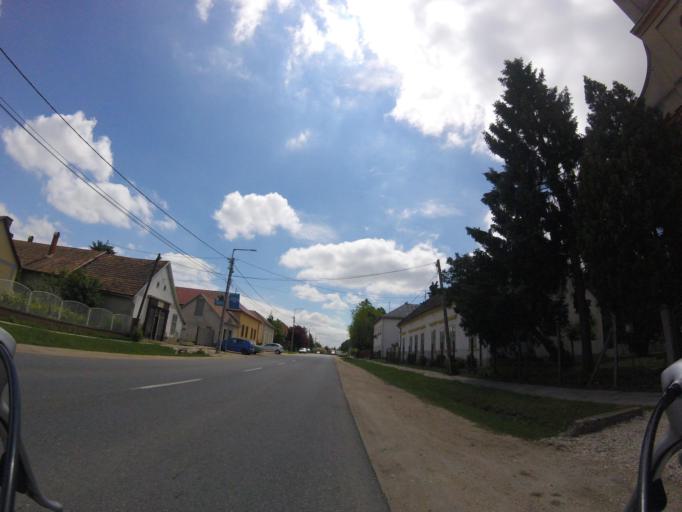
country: HU
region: Fejer
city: Seregelyes
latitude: 47.1079
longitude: 18.5837
